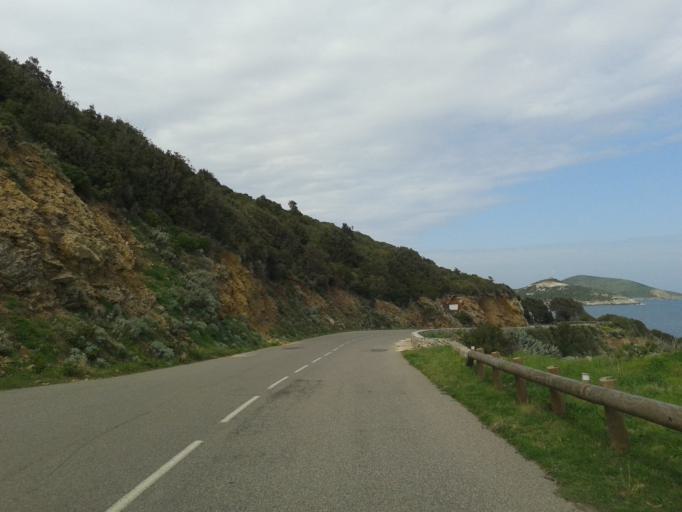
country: FR
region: Corsica
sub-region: Departement de la Haute-Corse
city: Brando
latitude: 42.9531
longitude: 9.4562
